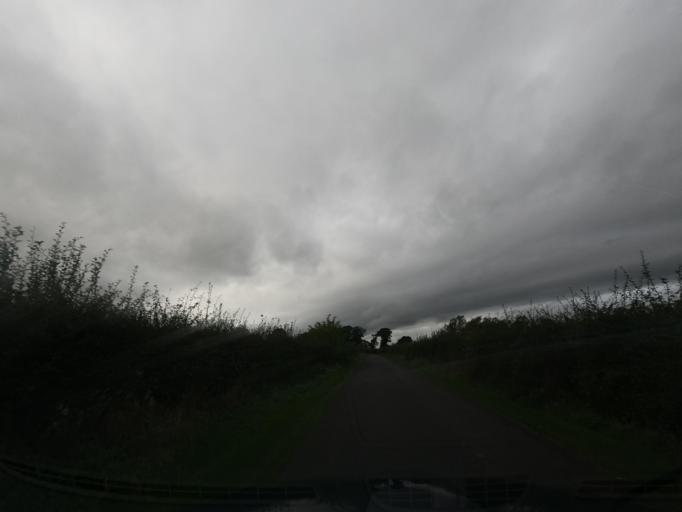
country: GB
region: England
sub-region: Northumberland
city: Doddington
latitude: 55.5962
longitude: -2.0237
